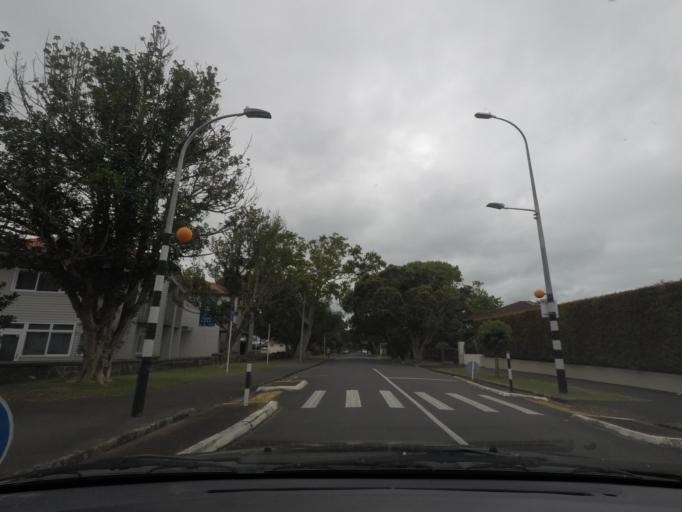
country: NZ
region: Auckland
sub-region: Auckland
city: Auckland
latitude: -36.8558
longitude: 174.7879
